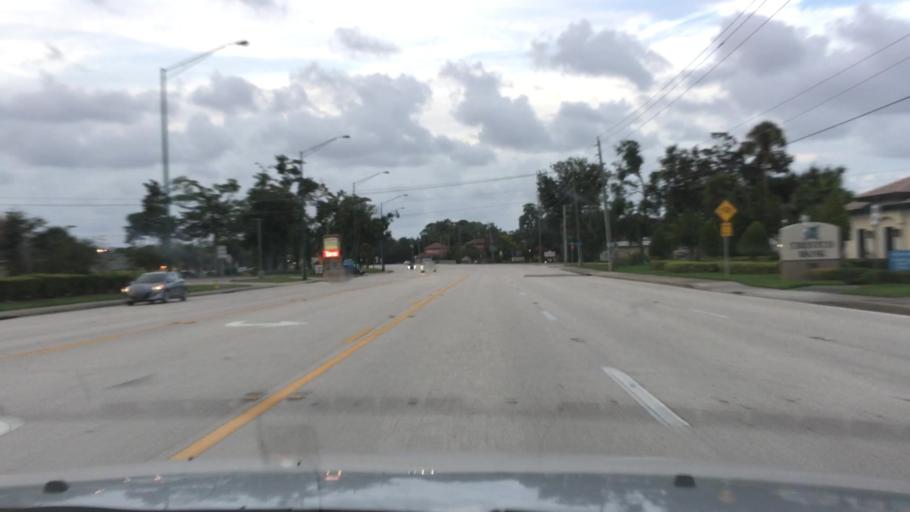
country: US
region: Florida
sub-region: Volusia County
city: Ormond Beach
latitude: 29.2815
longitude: -81.0826
